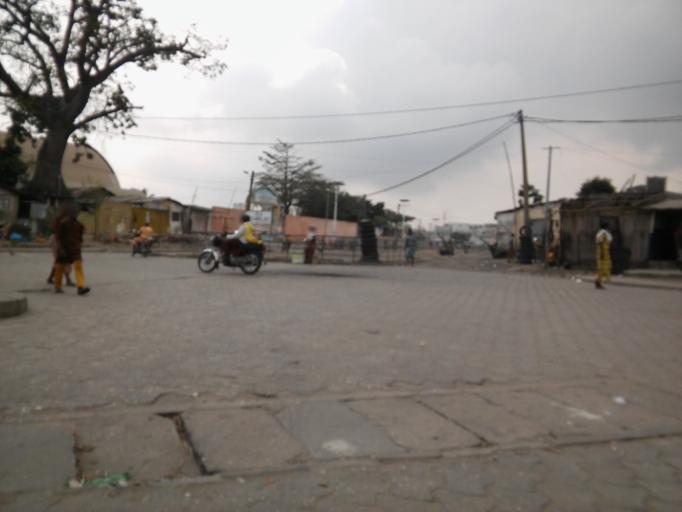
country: BJ
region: Littoral
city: Cotonou
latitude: 6.3863
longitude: 2.4226
